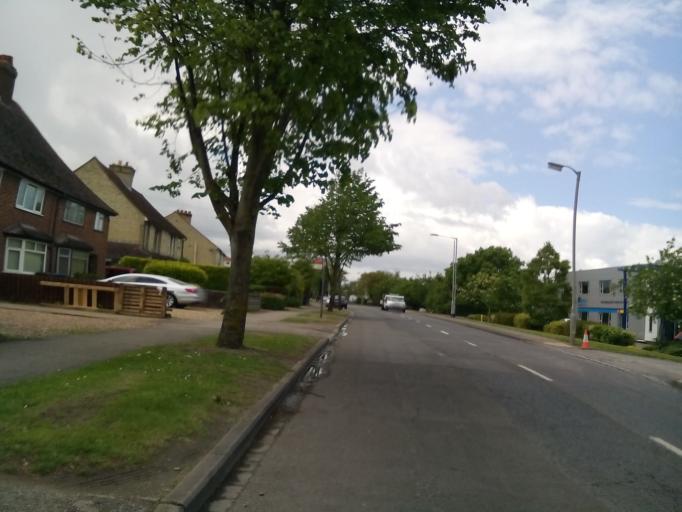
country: GB
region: England
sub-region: Cambridgeshire
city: Fulbourn
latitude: 52.1932
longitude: 0.1750
